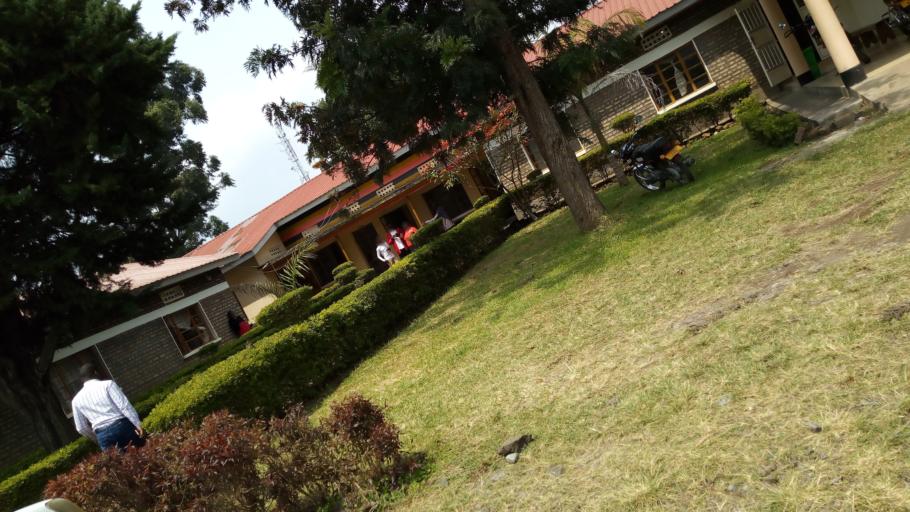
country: UG
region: Western Region
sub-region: Kisoro District
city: Kisoro
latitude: -1.2834
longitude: 29.6899
